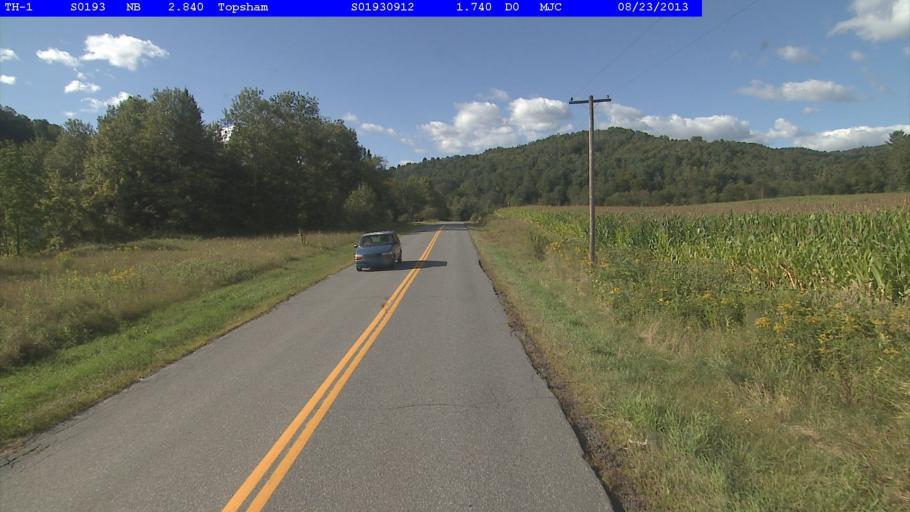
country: US
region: New Hampshire
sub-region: Grafton County
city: Haverhill
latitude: 44.0950
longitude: -72.2227
